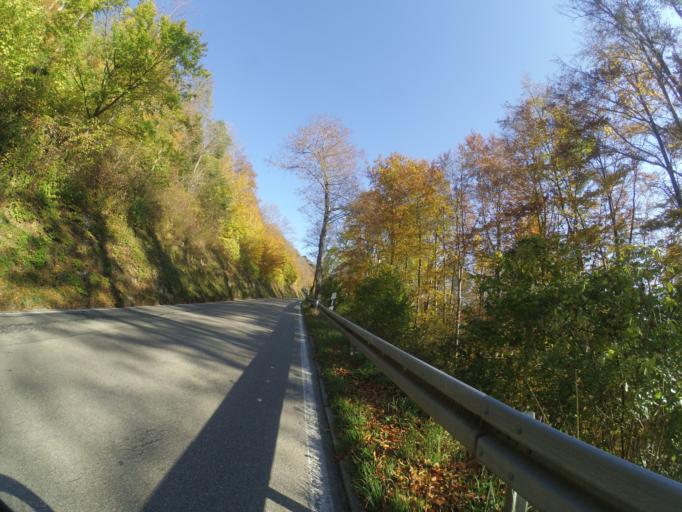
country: DE
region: Baden-Wuerttemberg
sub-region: Tuebingen Region
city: Blaubeuren
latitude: 48.4171
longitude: 9.7938
